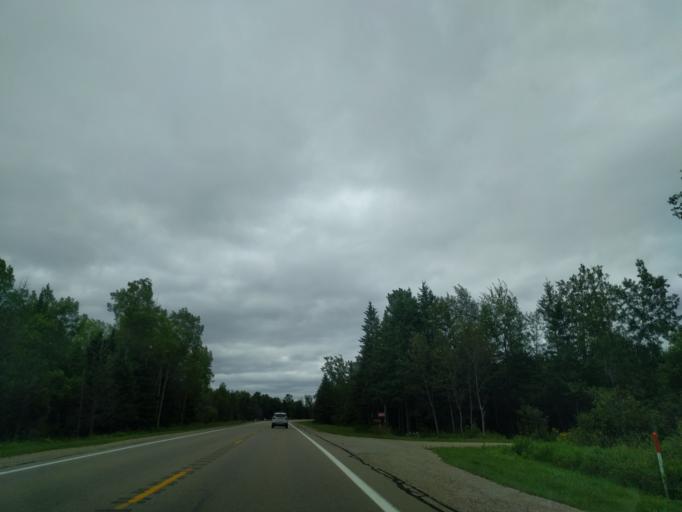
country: US
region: Michigan
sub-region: Delta County
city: Escanaba
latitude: 45.5110
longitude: -87.2878
